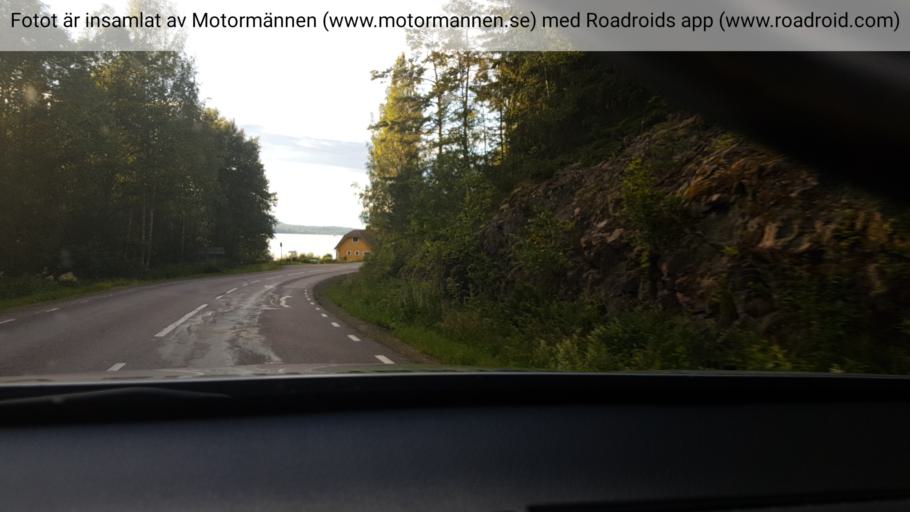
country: SE
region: Vaermland
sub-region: Sunne Kommun
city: Sunne
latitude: 59.9582
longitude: 13.1457
